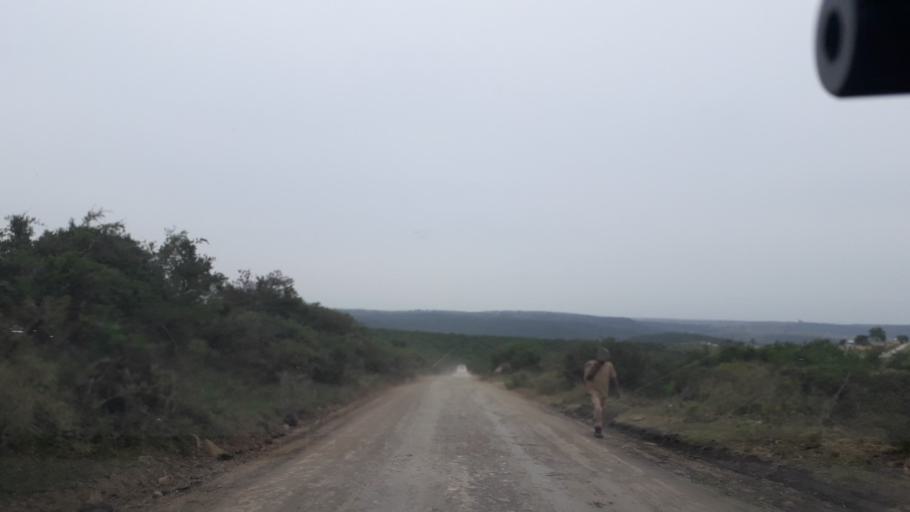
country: ZA
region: Eastern Cape
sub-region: Buffalo City Metropolitan Municipality
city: Bhisho
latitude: -32.7920
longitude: 27.3391
